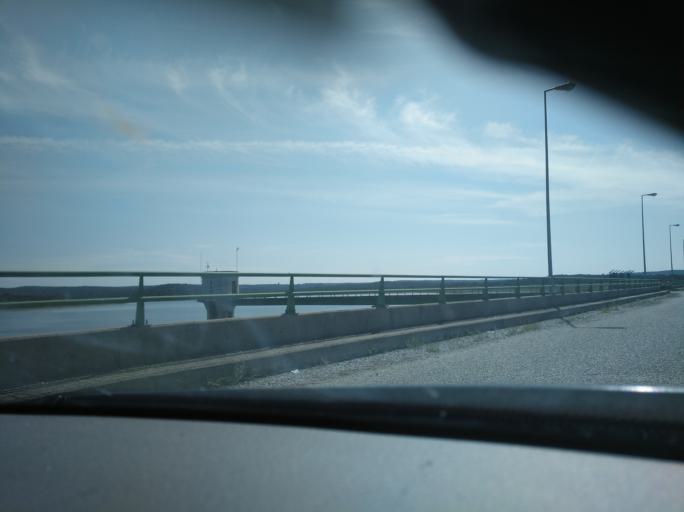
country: PT
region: Evora
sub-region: Montemor-O-Novo
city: Montemor-o-Novo
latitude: 38.6611
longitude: -8.0978
